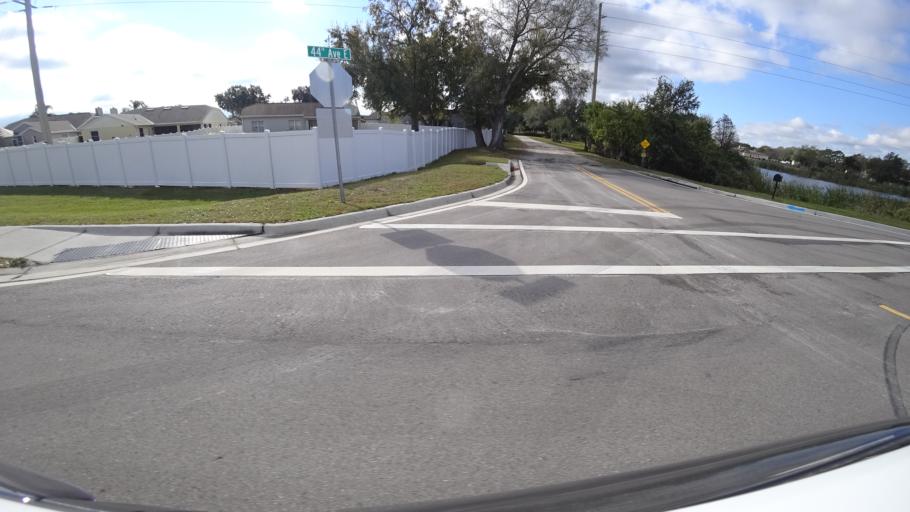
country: US
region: Florida
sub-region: Manatee County
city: Samoset
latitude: 27.4617
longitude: -82.5137
